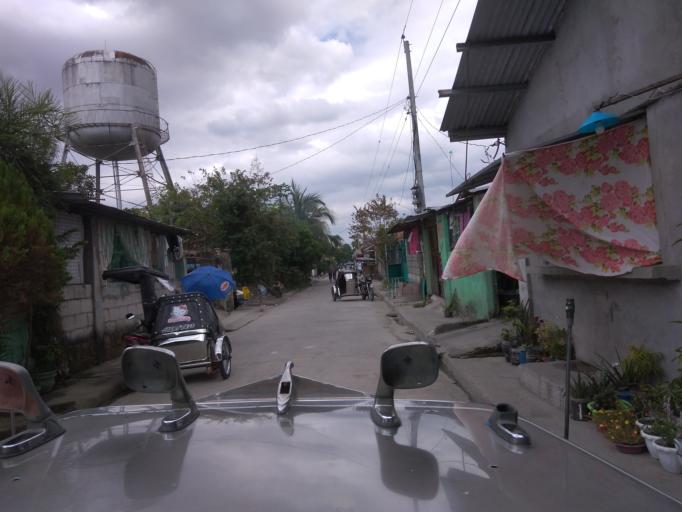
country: PH
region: Central Luzon
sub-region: Province of Pampanga
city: Pandacaqui
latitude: 15.1789
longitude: 120.6548
